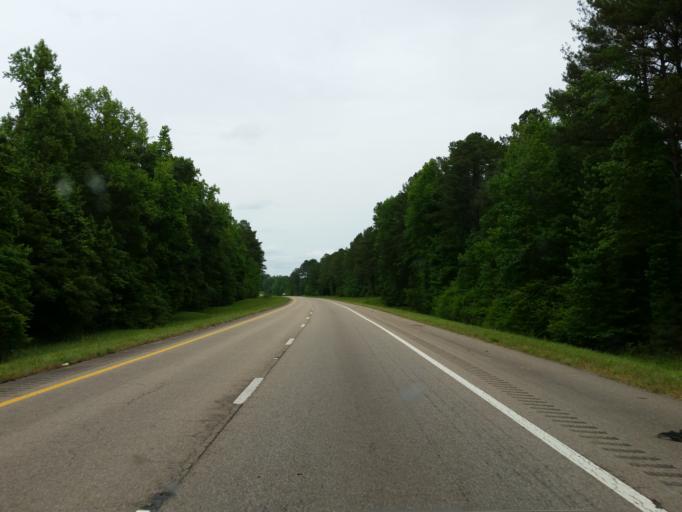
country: US
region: Mississippi
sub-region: Clarke County
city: Stonewall
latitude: 31.9781
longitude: -88.9531
